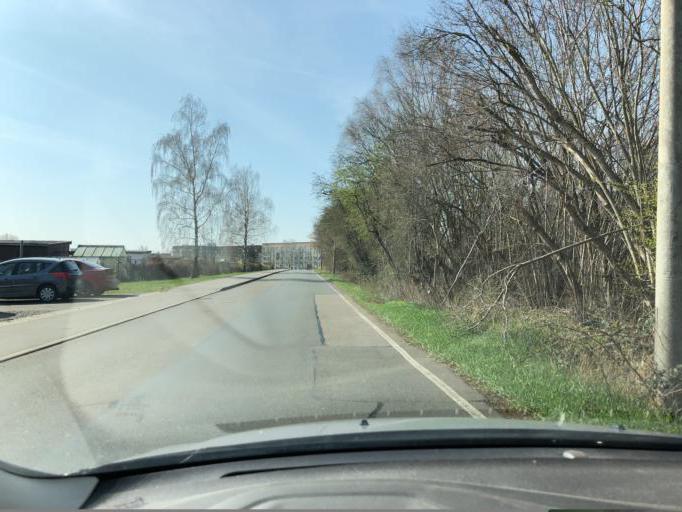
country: DE
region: Saxony
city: Rackwitz
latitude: 51.3871
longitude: 12.4222
